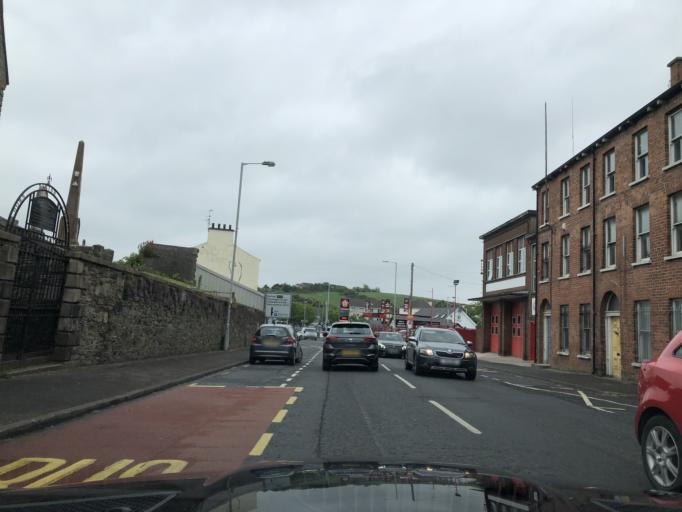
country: GB
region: Northern Ireland
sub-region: Down District
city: Downpatrick
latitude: 54.3295
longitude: -5.7157
